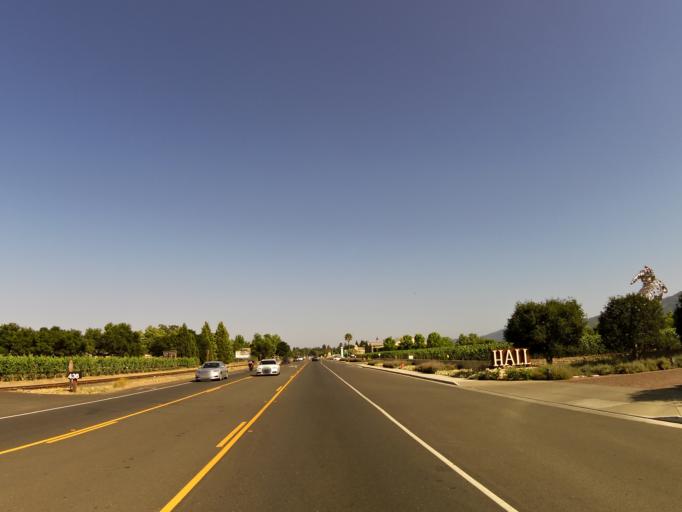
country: US
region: California
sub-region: Napa County
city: Saint Helena
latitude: 38.4905
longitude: -122.4520
